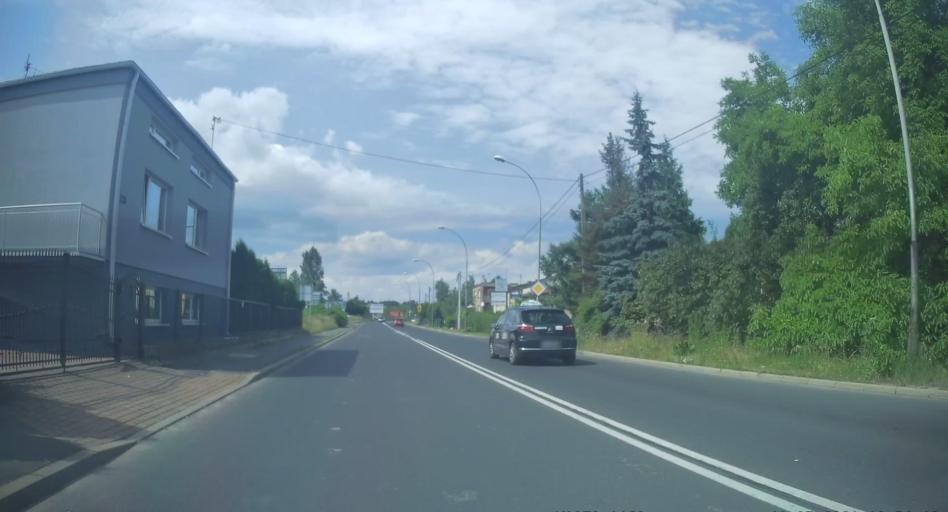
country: PL
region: Silesian Voivodeship
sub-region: Czestochowa
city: Czestochowa
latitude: 50.8029
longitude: 19.0818
